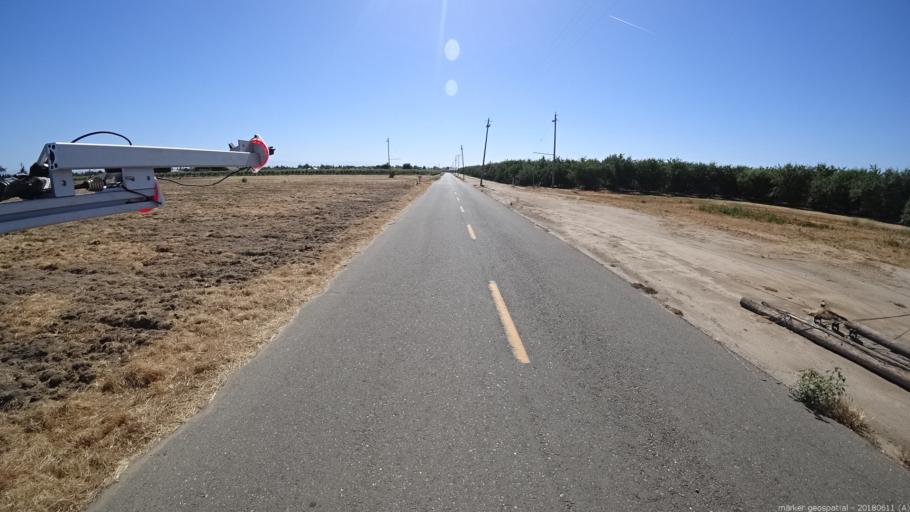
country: US
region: California
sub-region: Madera County
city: Madera
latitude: 36.9492
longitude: -120.1064
